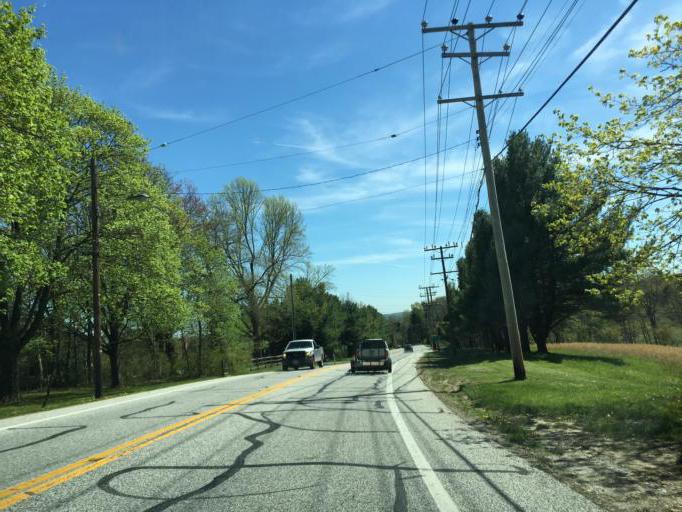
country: US
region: Maryland
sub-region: Baltimore County
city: Hunt Valley
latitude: 39.5864
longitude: -76.6631
